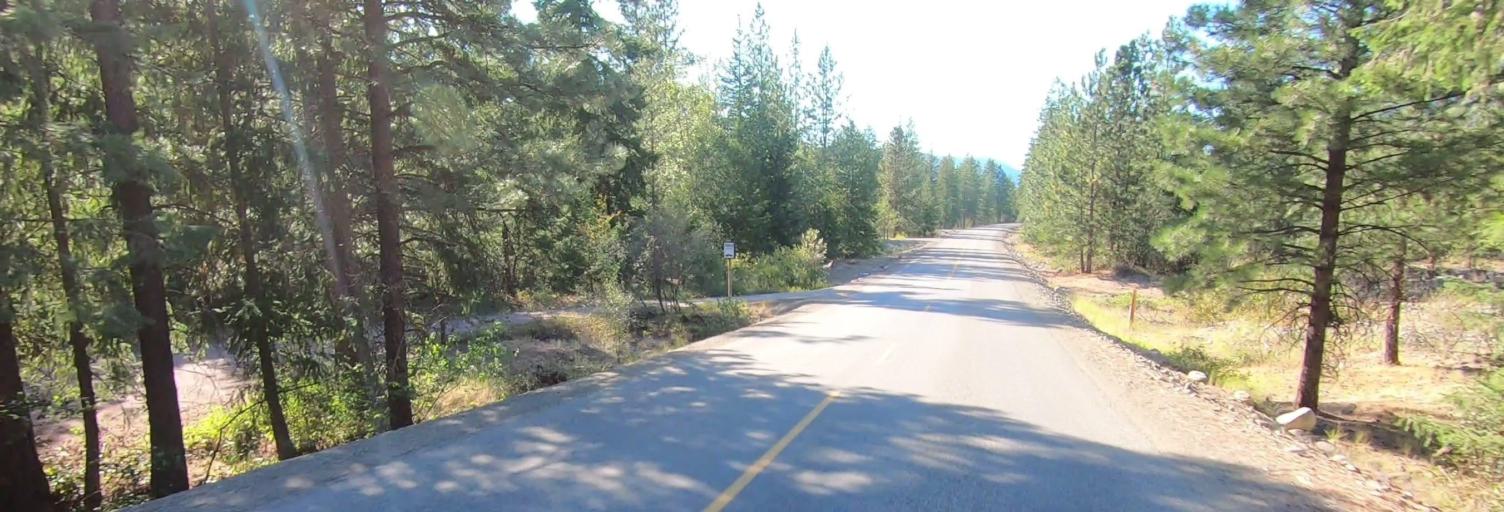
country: US
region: Washington
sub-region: Chelan County
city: Granite Falls
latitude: 48.5795
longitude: -120.3750
